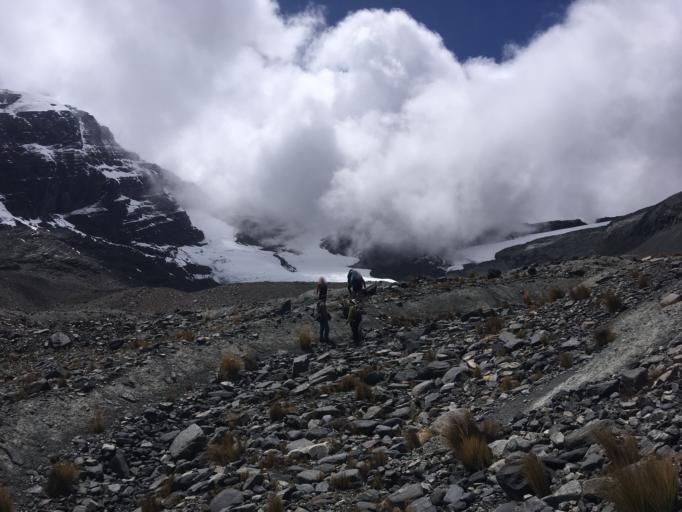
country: BO
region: La Paz
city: La Paz
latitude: -16.3977
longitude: -67.9509
